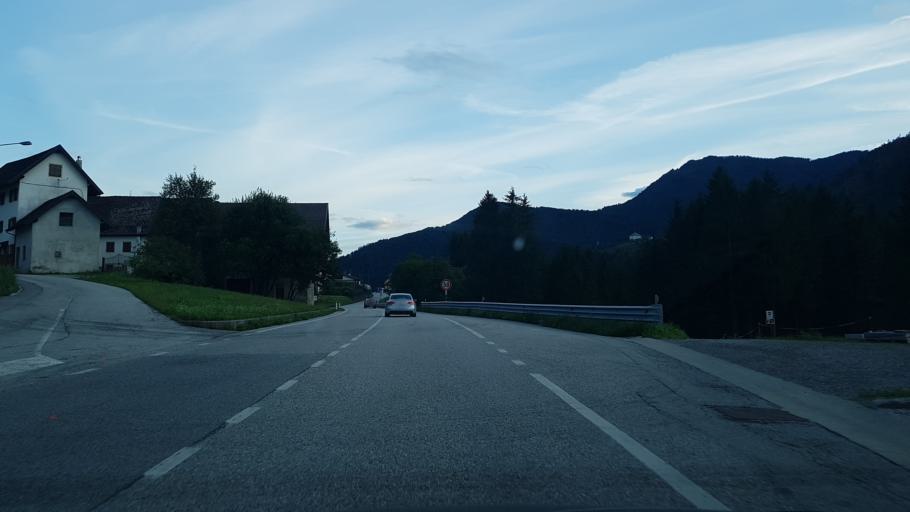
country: IT
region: Friuli Venezia Giulia
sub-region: Provincia di Udine
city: Ovaro
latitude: 46.4932
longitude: 12.8660
